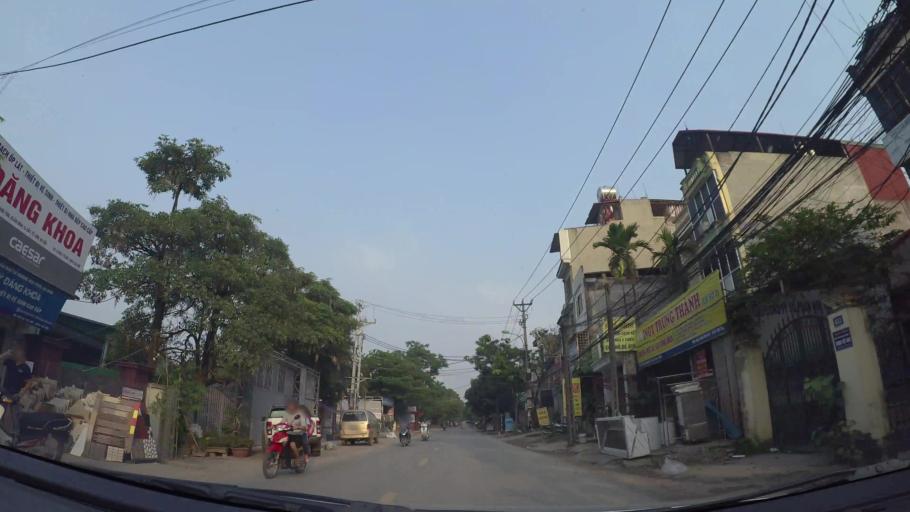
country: VN
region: Ha Noi
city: Tay Ho
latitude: 21.0766
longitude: 105.7927
